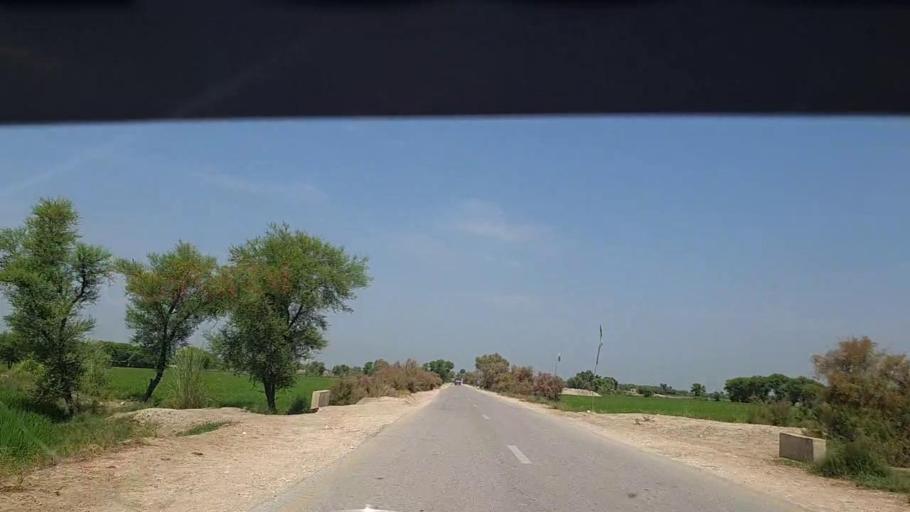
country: PK
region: Sindh
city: Thul
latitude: 28.1444
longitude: 68.8177
